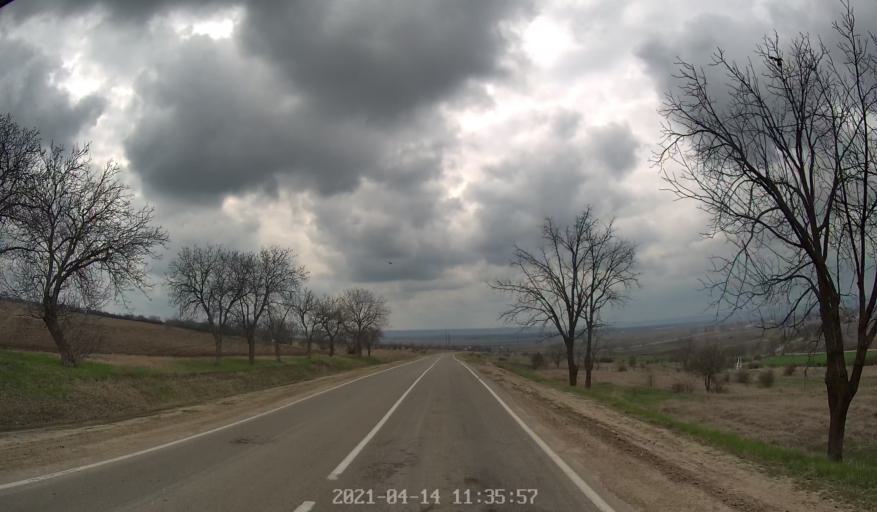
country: MD
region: Criuleni
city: Criuleni
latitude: 47.1645
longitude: 29.1633
